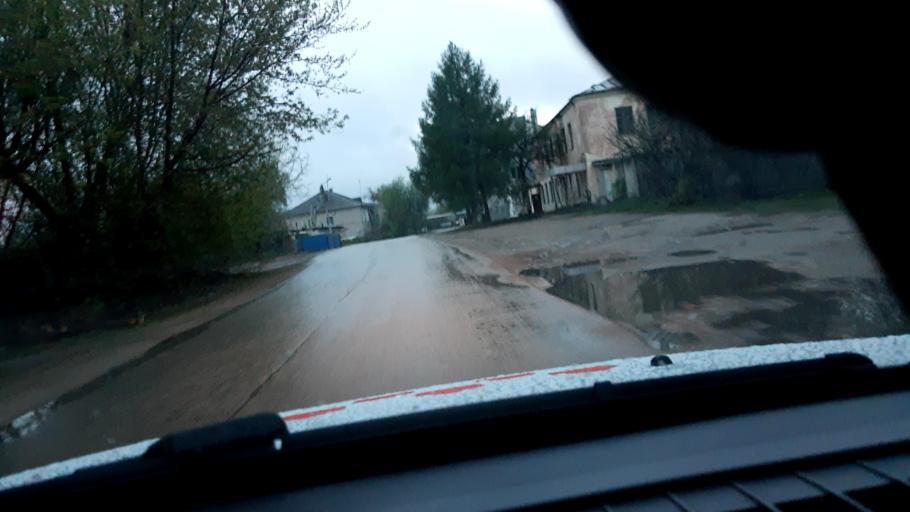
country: RU
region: Nizjnij Novgorod
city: Bor
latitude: 56.3629
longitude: 44.0533
